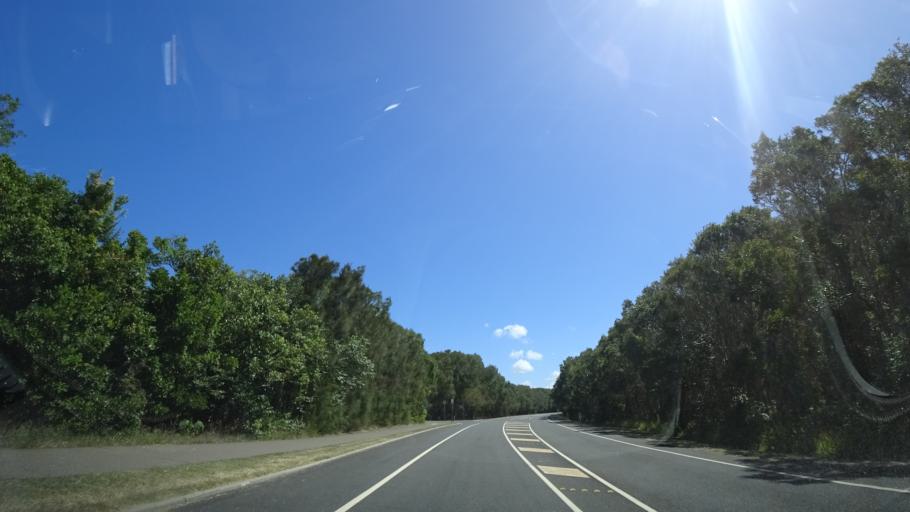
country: AU
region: Queensland
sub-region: Sunshine Coast
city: Mooloolaba
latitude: -26.6282
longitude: 153.0999
